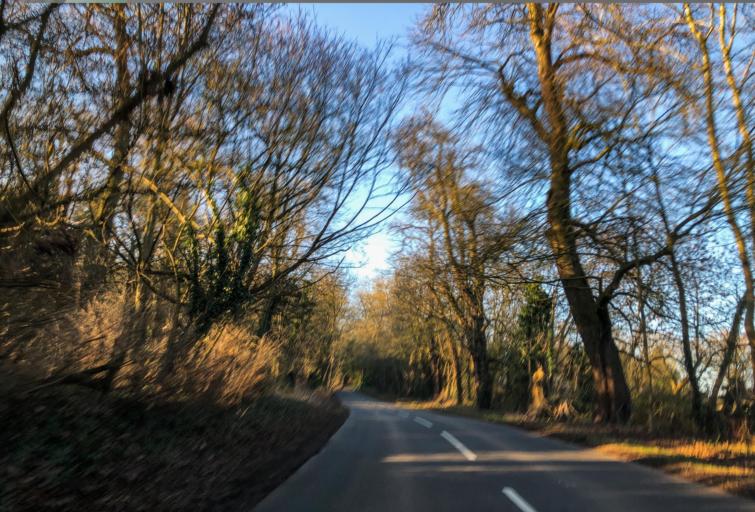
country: GB
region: England
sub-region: Warwickshire
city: Wellesbourne Mountford
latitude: 52.2232
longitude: -1.5425
